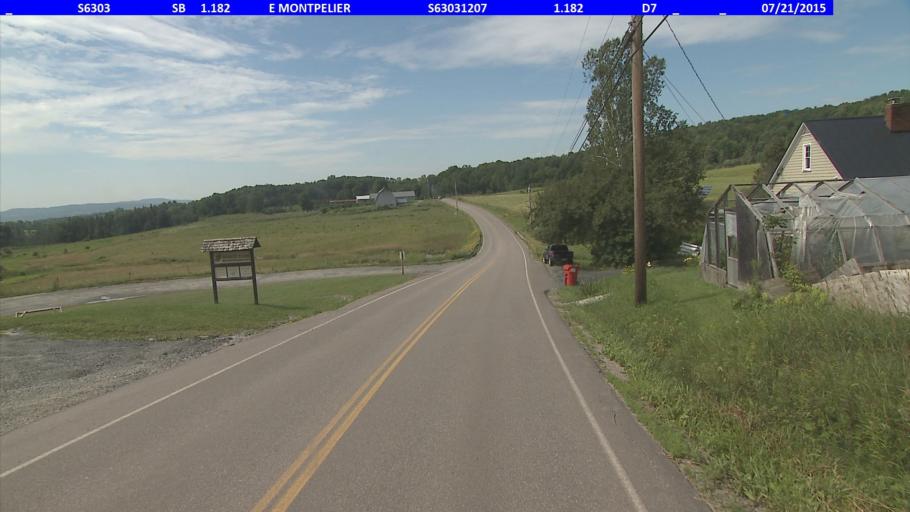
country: US
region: Vermont
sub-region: Washington County
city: Montpelier
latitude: 44.2866
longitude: -72.5437
